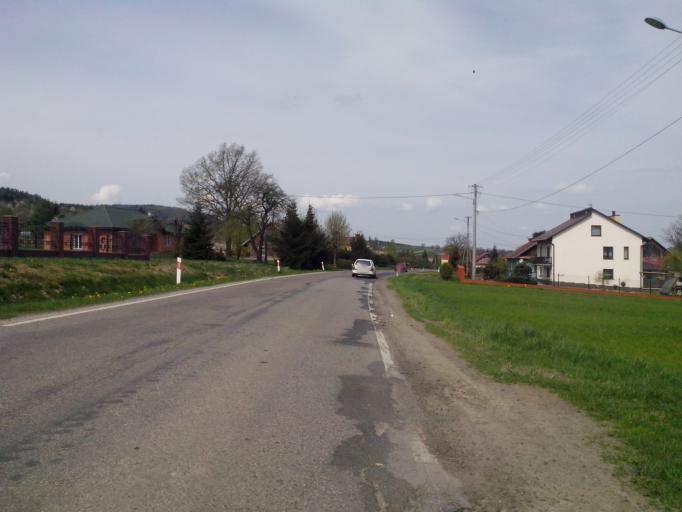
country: PL
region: Subcarpathian Voivodeship
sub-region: Powiat strzyzowski
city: Jawornik
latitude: 49.8085
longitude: 21.8518
